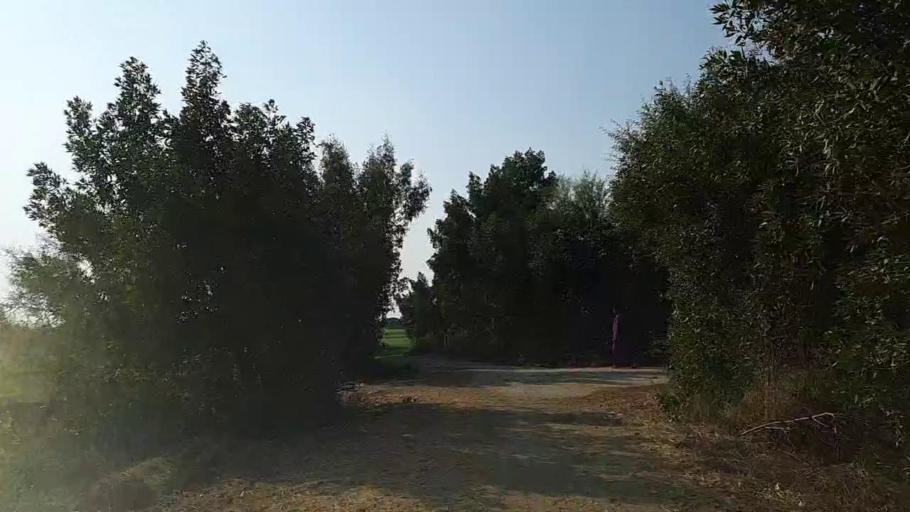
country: PK
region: Sindh
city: Jam Sahib
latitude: 26.2900
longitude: 68.5588
